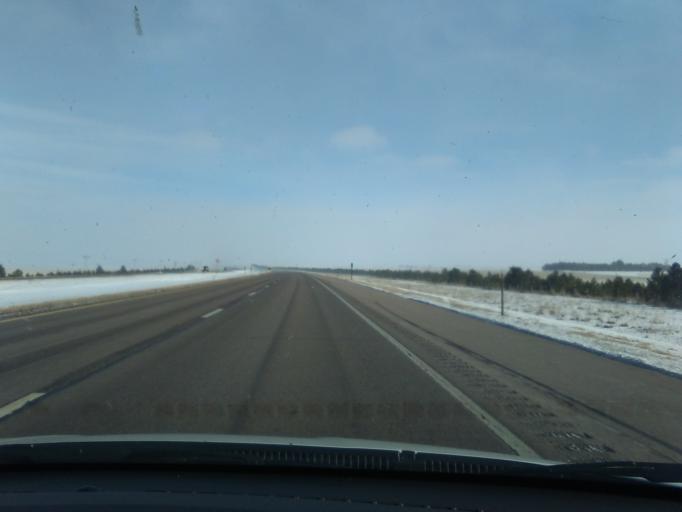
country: US
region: Nebraska
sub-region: Kimball County
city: Kimball
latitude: 41.1927
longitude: -103.7686
